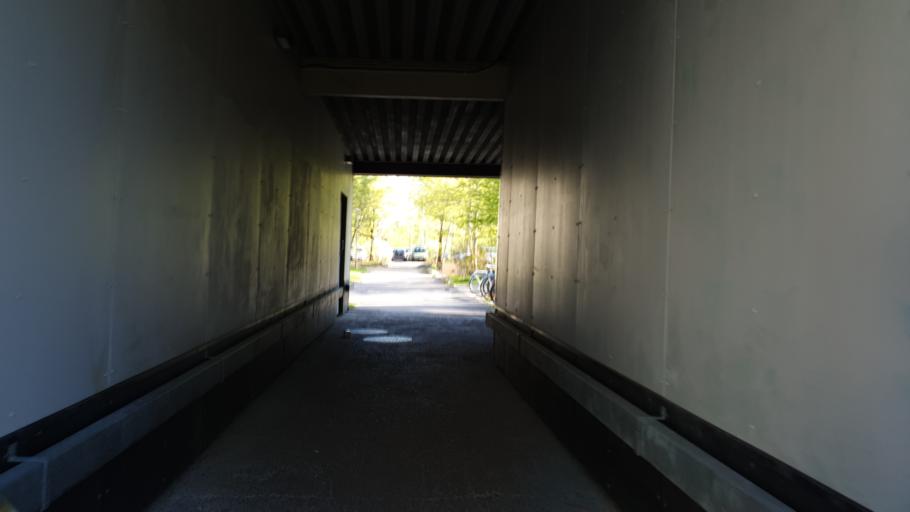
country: FI
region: Uusimaa
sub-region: Helsinki
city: Teekkarikylae
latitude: 60.2435
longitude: 24.8564
